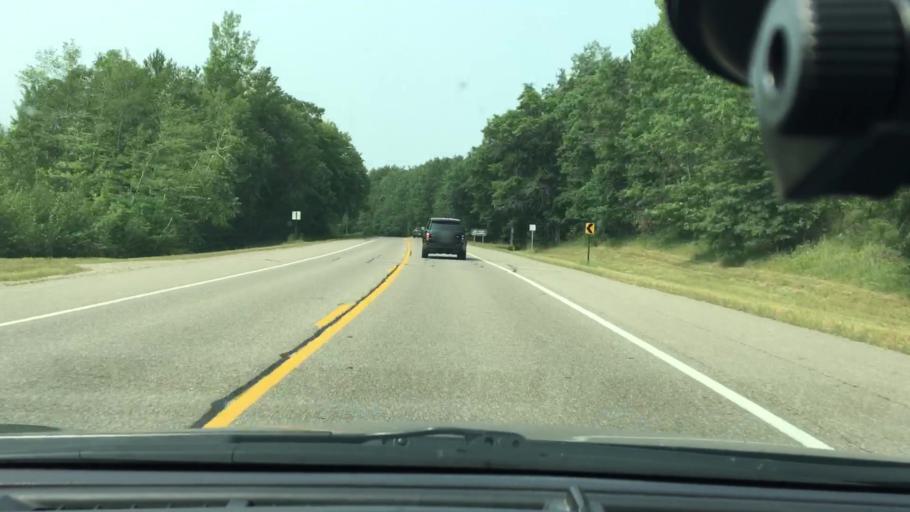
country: US
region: Minnesota
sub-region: Cass County
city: East Gull Lake
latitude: 46.3831
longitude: -94.3274
